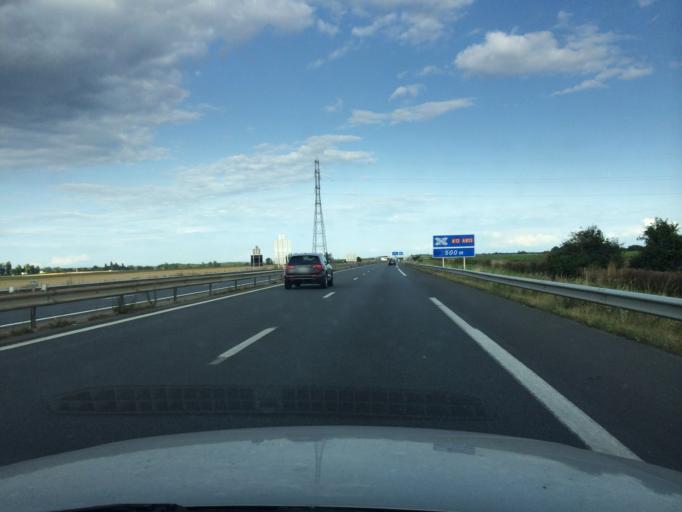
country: FR
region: Lower Normandy
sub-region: Departement du Calvados
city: Demouville
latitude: 49.1681
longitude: -0.2604
